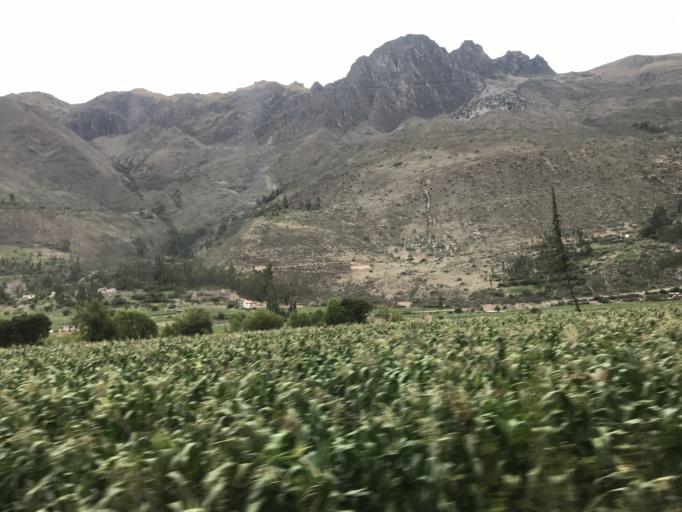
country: PE
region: Cusco
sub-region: Provincia de Urubamba
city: Ollantaytambo
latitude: -13.2494
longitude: -72.2891
